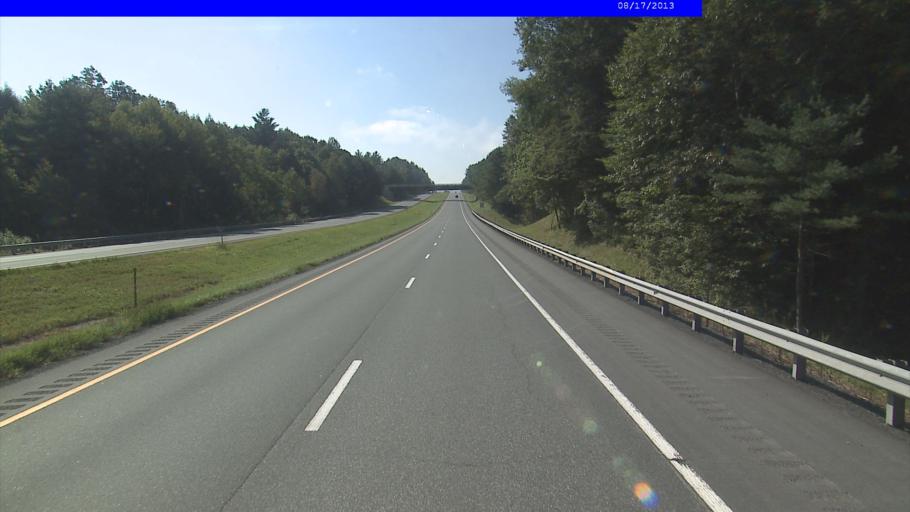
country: US
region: Vermont
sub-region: Windsor County
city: White River Junction
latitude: 43.6150
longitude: -72.3471
